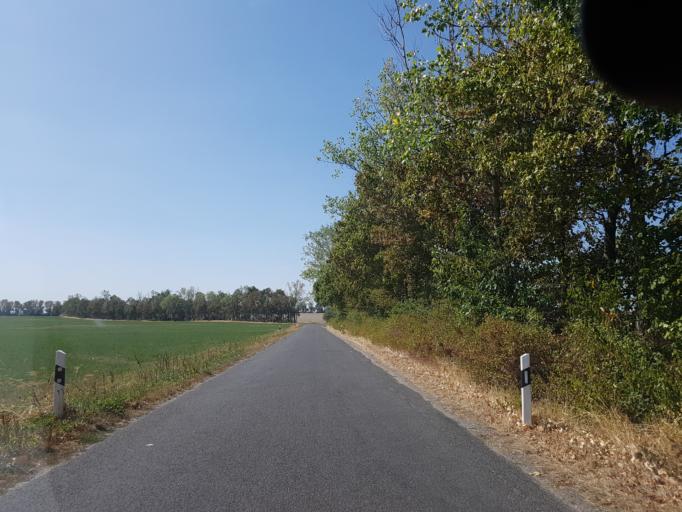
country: DE
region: Saxony-Anhalt
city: Kropstadt
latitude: 52.0256
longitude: 12.7522
